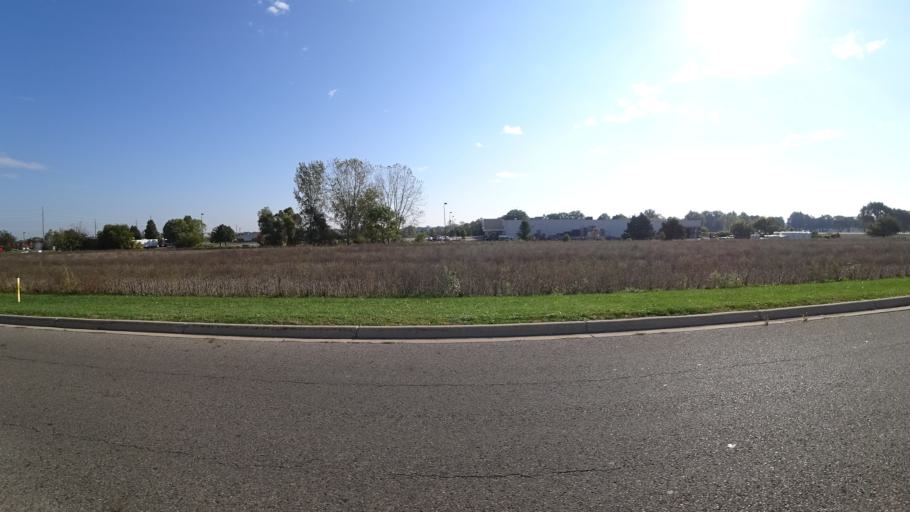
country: US
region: Michigan
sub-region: Saint Joseph County
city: Three Rivers
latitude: 41.9307
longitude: -85.6557
